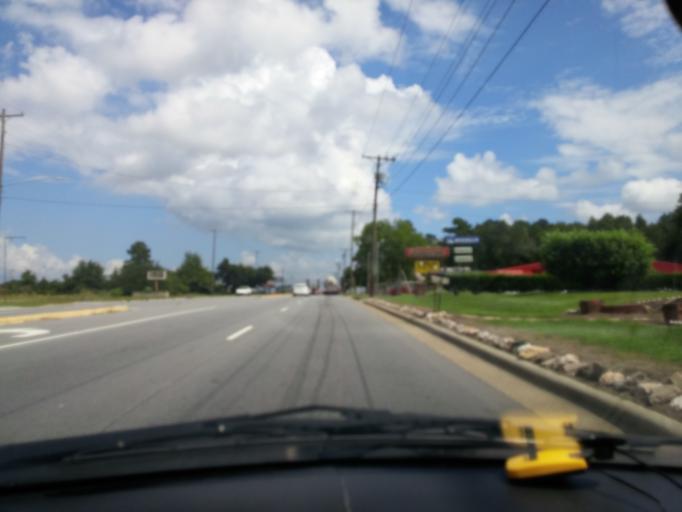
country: US
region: North Carolina
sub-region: Lenoir County
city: Kinston
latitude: 35.2738
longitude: -77.5667
